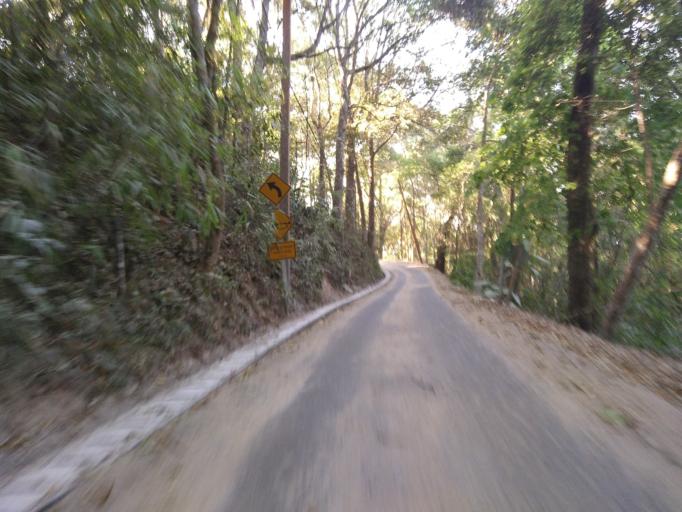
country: TH
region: Chiang Mai
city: Chiang Mai
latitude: 18.8111
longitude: 98.8919
